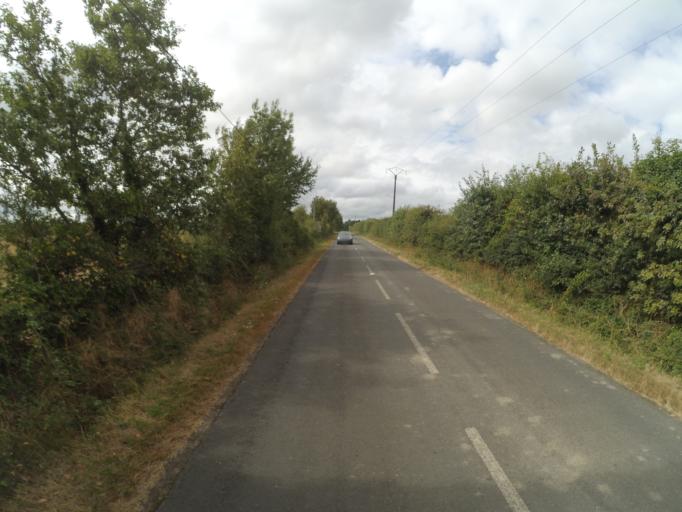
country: FR
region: Pays de la Loire
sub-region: Departement de la Loire-Atlantique
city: La Limouziniere
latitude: 47.0322
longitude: -1.5776
